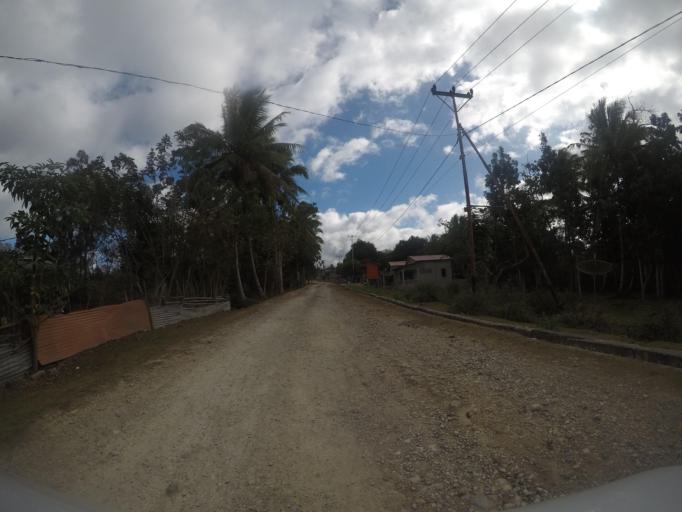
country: TL
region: Lautem
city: Lospalos
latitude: -8.5671
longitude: 126.8856
